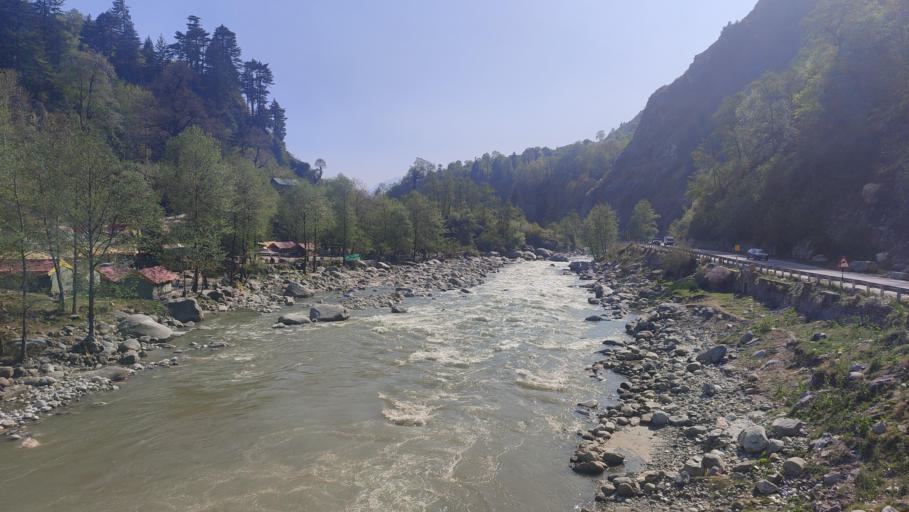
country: IN
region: Himachal Pradesh
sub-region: Kulu
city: Nagar
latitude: 32.1815
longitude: 77.1827
